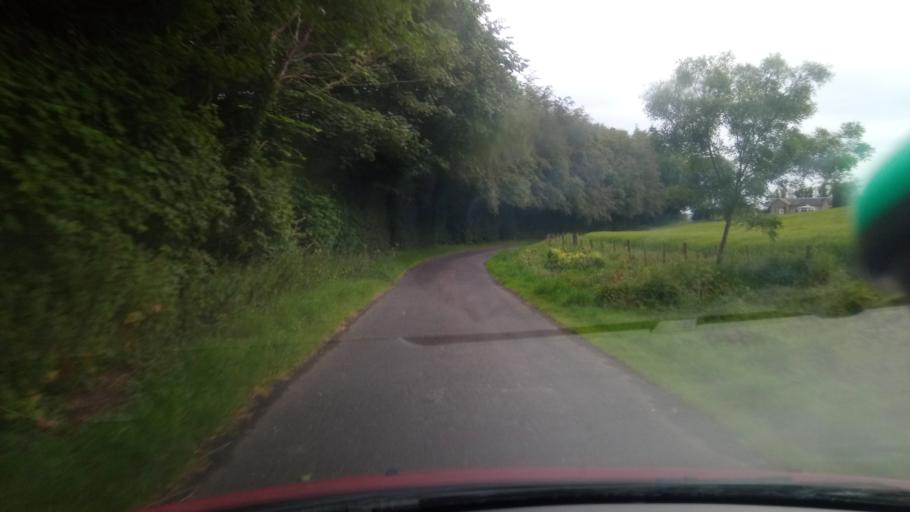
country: GB
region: Scotland
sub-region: The Scottish Borders
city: Saint Boswells
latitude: 55.4762
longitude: -2.6595
